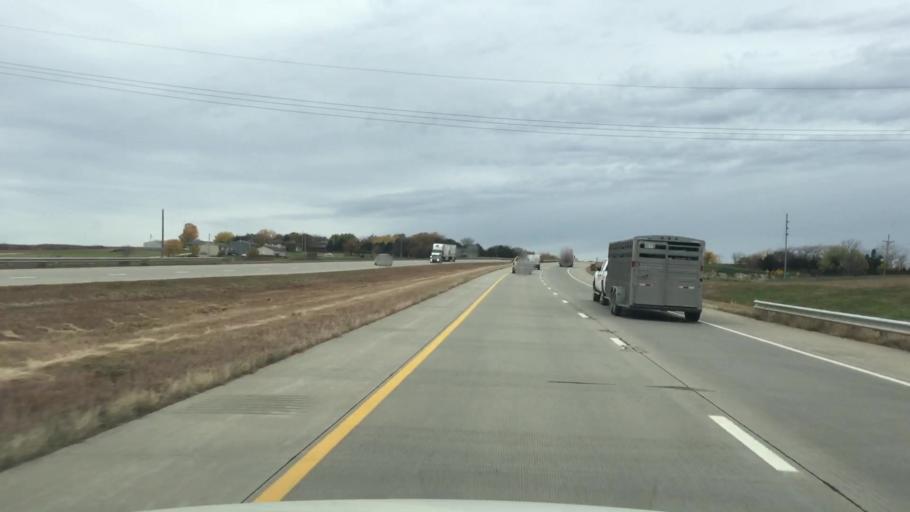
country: US
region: Kansas
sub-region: Wabaunsee County
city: Alma
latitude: 39.0583
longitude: -96.1652
